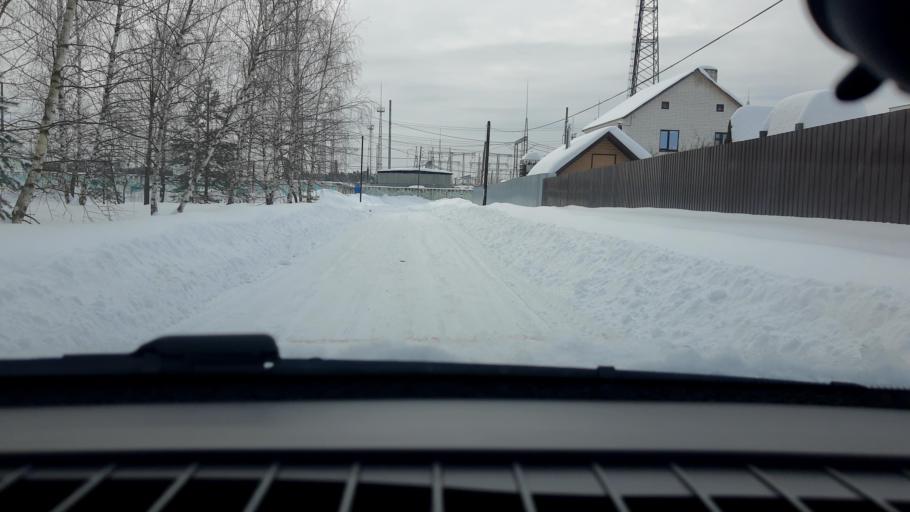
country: RU
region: Nizjnij Novgorod
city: Lukino
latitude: 56.3967
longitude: 43.7021
